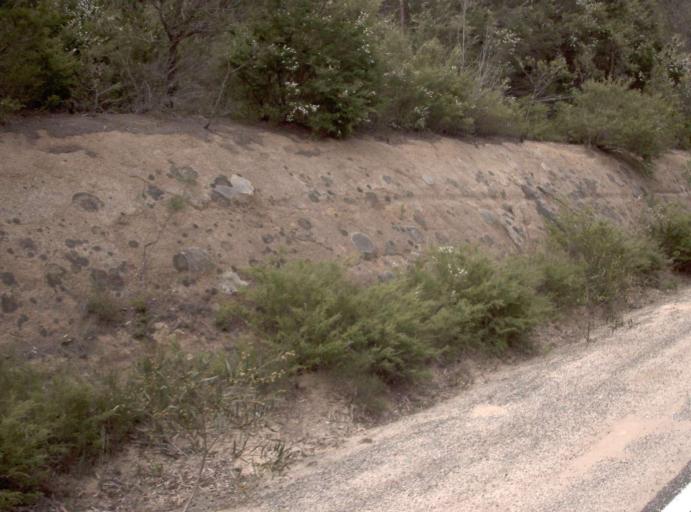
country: AU
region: New South Wales
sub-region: Bega Valley
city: Eden
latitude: -37.4081
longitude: 149.6592
